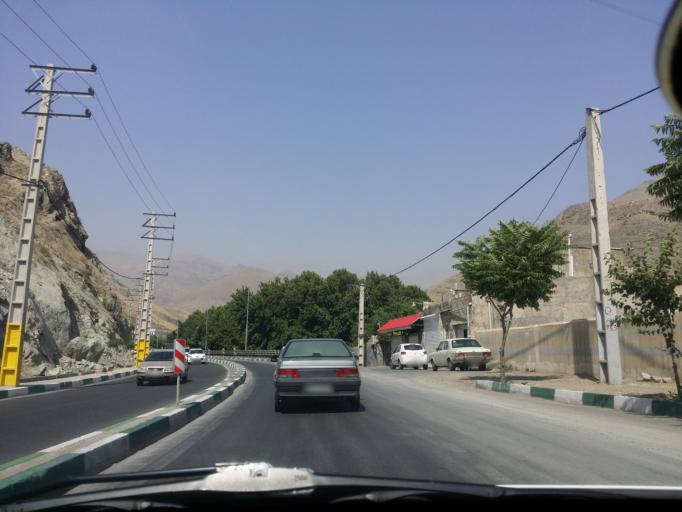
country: IR
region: Alborz
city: Karaj
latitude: 35.8306
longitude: 51.0372
